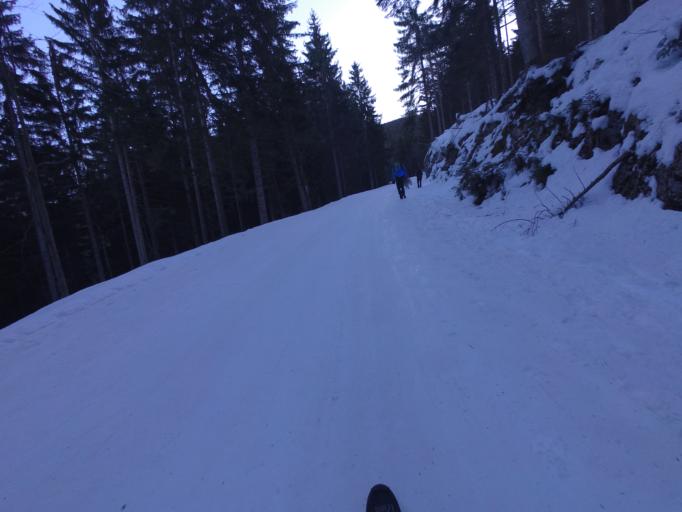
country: AT
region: Salzburg
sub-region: Politischer Bezirk Hallein
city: Scheffau am Tennengebirge
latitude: 47.6401
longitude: 13.2468
